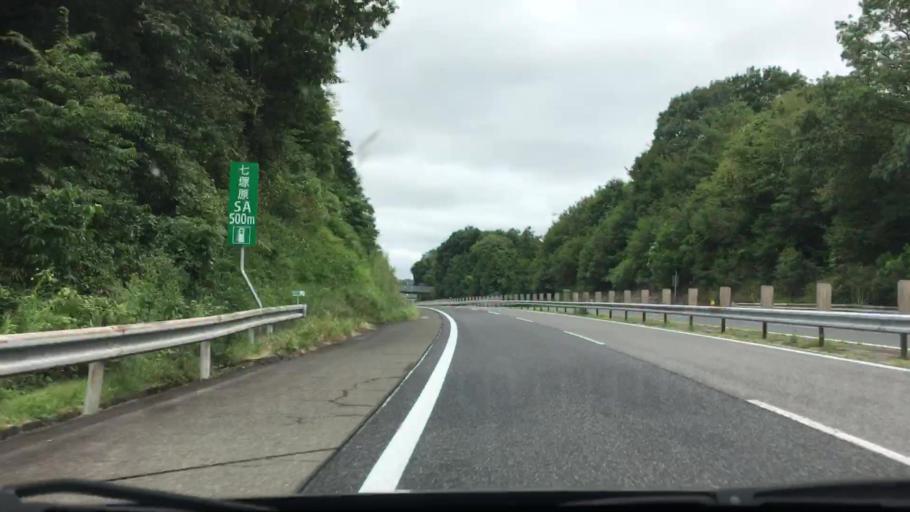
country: JP
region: Hiroshima
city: Shobara
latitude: 34.8315
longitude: 132.9650
